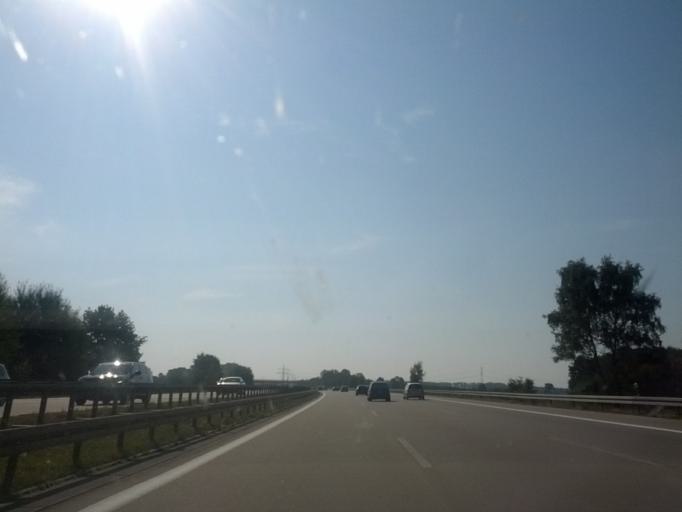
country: DE
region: Berlin
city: Hellersdorf
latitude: 52.5679
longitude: 13.6487
